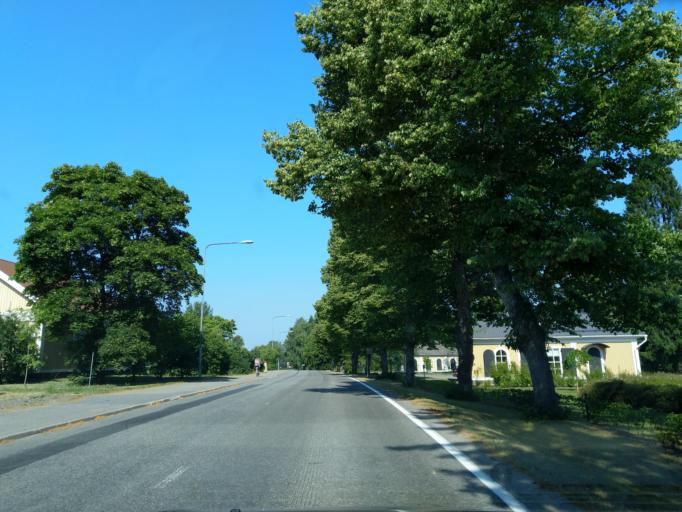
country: FI
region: Satakunta
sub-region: Pori
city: Noormarkku
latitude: 61.5920
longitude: 21.8768
